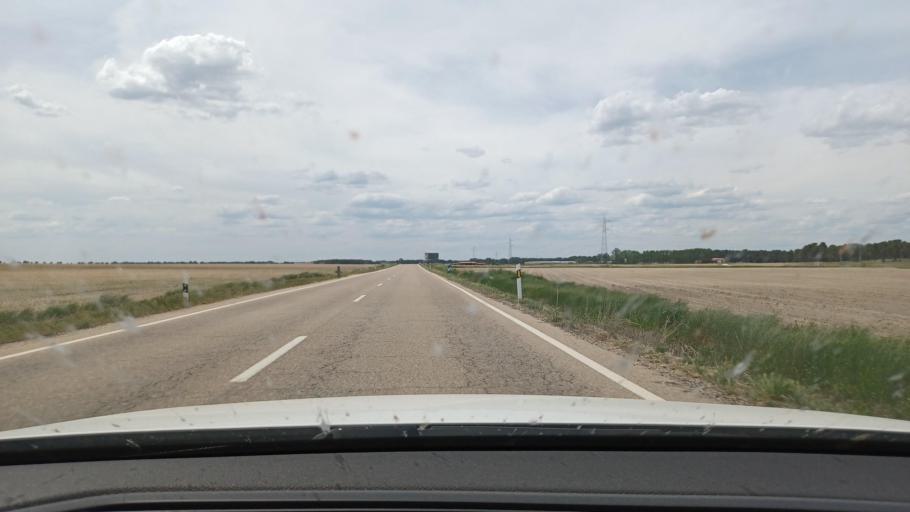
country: ES
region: Castille and Leon
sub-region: Provincia de Segovia
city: Cantalejo
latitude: 41.2666
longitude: -3.9451
